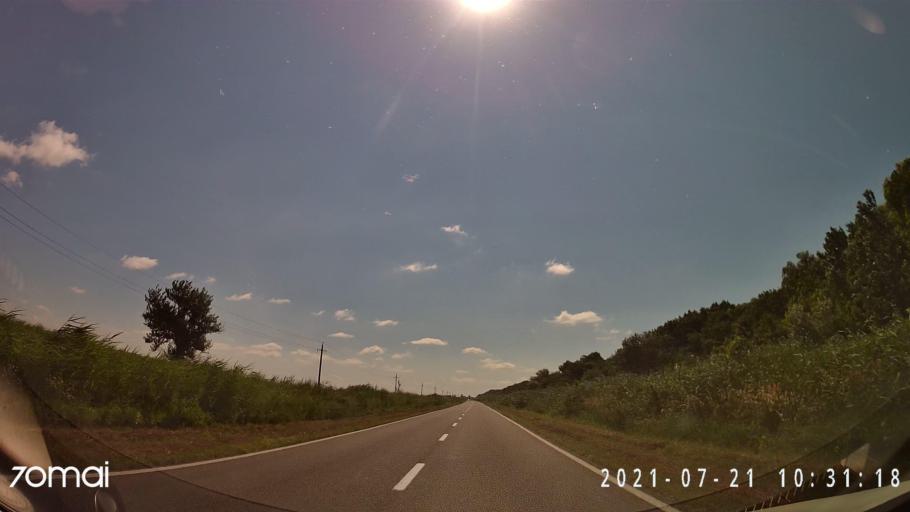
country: RO
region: Tulcea
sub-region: Comuna Luncavita
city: Rachelu
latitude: 45.3093
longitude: 28.3977
